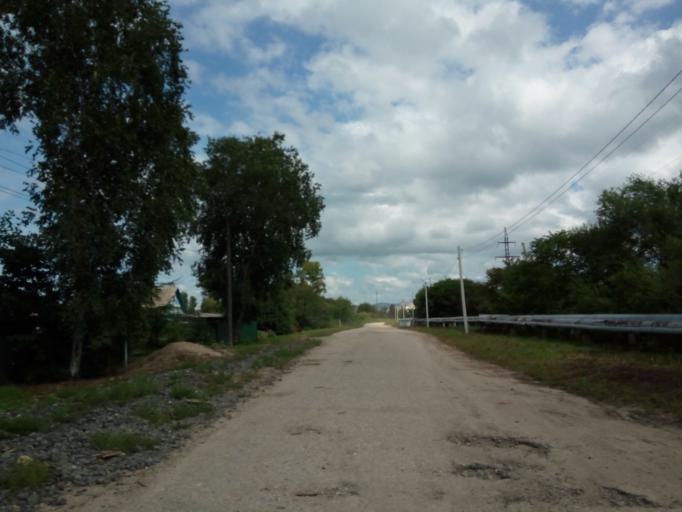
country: RU
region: Primorskiy
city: Dal'nerechensk
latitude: 45.9502
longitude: 133.8191
